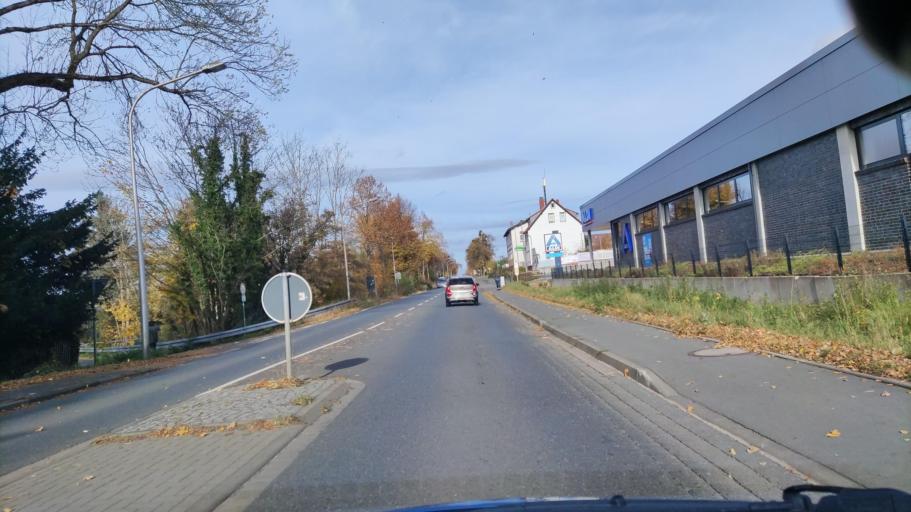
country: DE
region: Lower Saxony
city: Goslar
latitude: 51.9162
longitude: 10.4174
